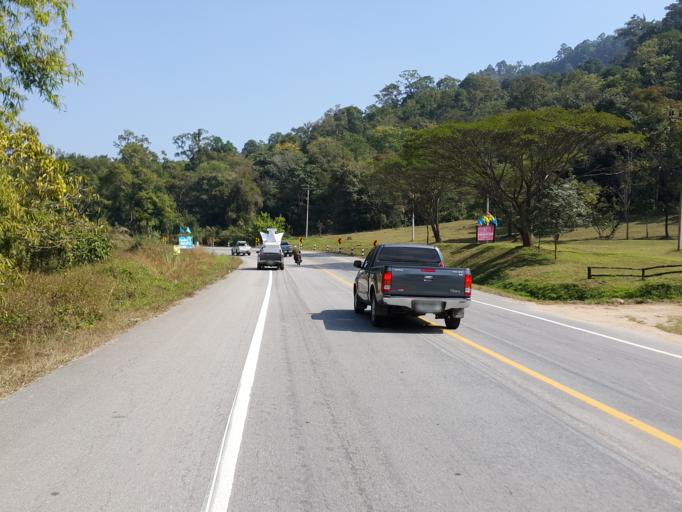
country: TH
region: Lampang
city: Wang Nuea
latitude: 19.0953
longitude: 99.4385
